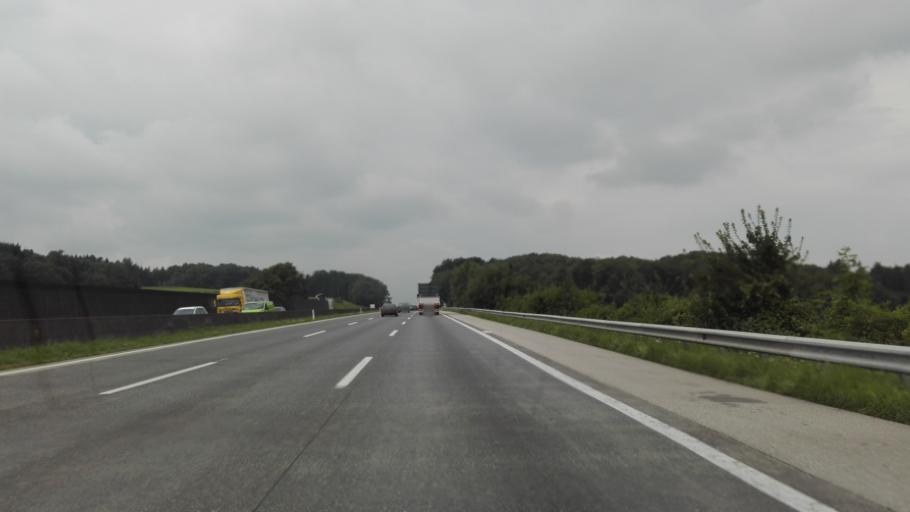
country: AT
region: Lower Austria
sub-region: Politischer Bezirk Scheibbs
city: Wieselburg
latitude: 48.1622
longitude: 15.1402
